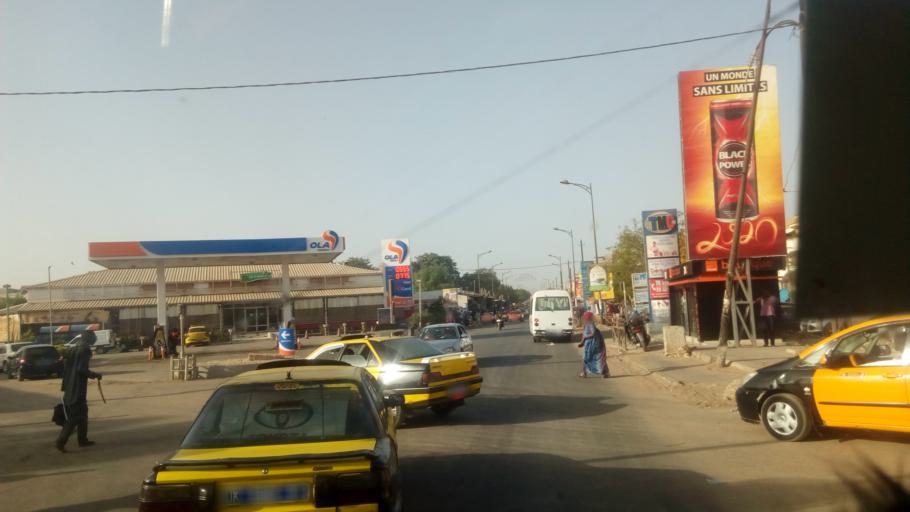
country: SN
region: Dakar
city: Dakar
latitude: 14.7046
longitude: -17.4468
